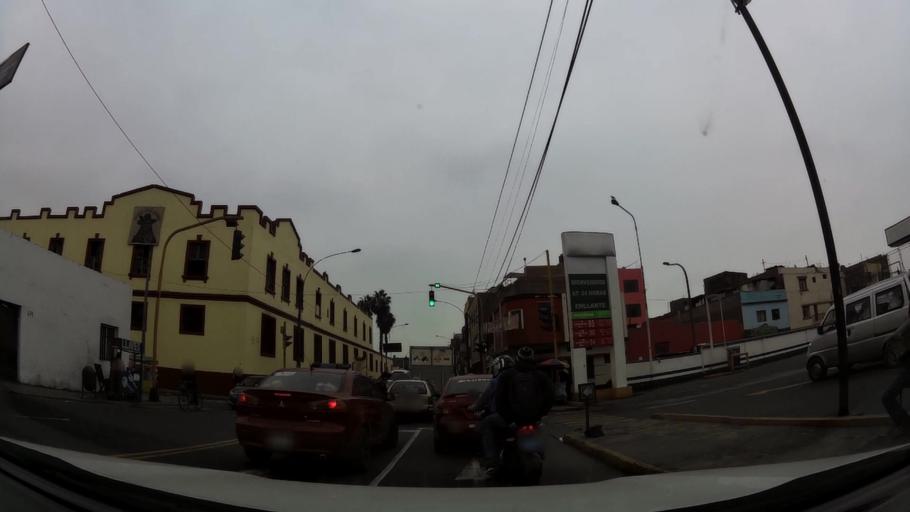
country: PE
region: Lima
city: Lima
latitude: -12.0492
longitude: -77.0129
